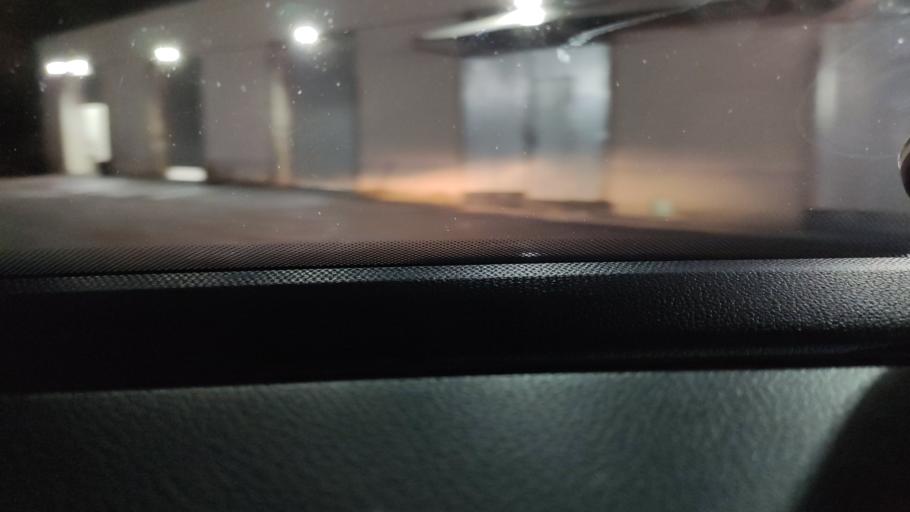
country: RU
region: Moscow
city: Zapadnoye Degunino
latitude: 55.8449
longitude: 37.5308
